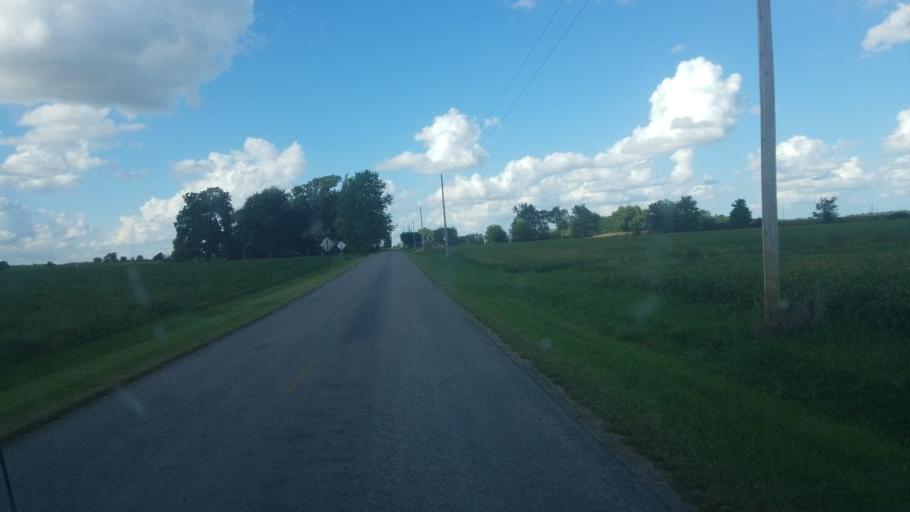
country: US
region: Ohio
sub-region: Hardin County
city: Kenton
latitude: 40.6911
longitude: -83.6923
